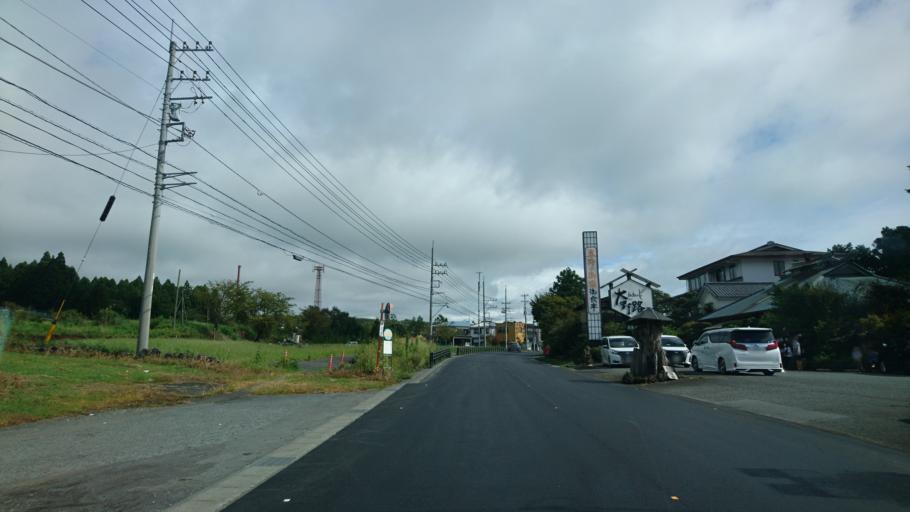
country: JP
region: Shizuoka
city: Gotemba
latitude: 35.2593
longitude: 138.8606
